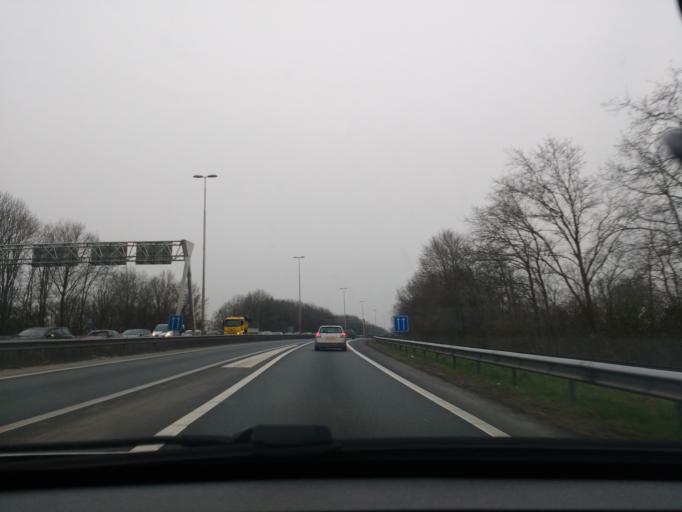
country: NL
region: Gelderland
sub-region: Gemeente Barneveld
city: Barneveld
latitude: 52.1640
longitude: 5.5658
